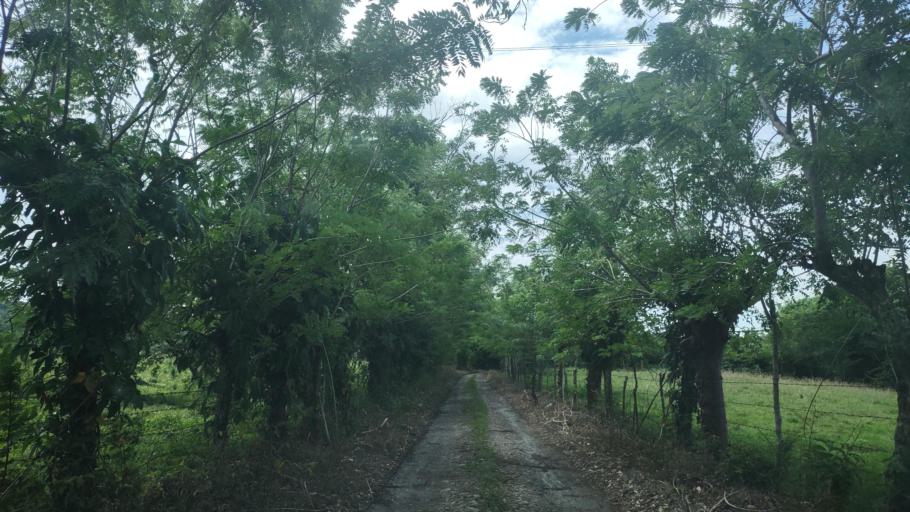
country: MX
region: Veracruz
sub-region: Atzalan
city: Colonias Pedernales
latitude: 20.0613
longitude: -97.0090
